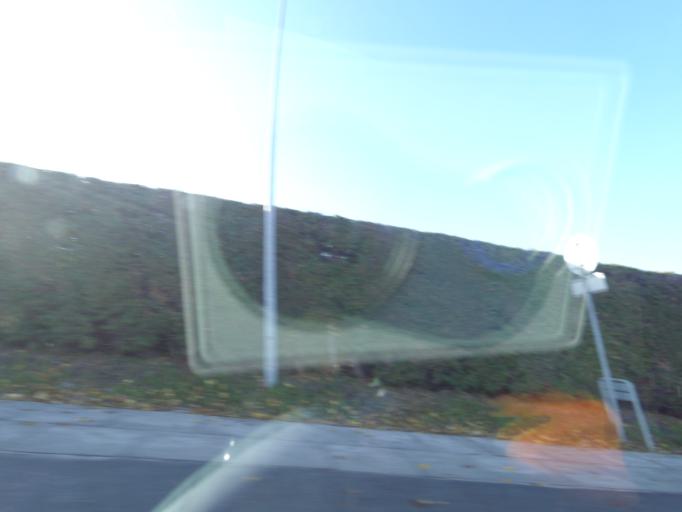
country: DK
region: South Denmark
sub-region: Odense Kommune
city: Hojby
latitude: 55.3399
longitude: 10.4334
